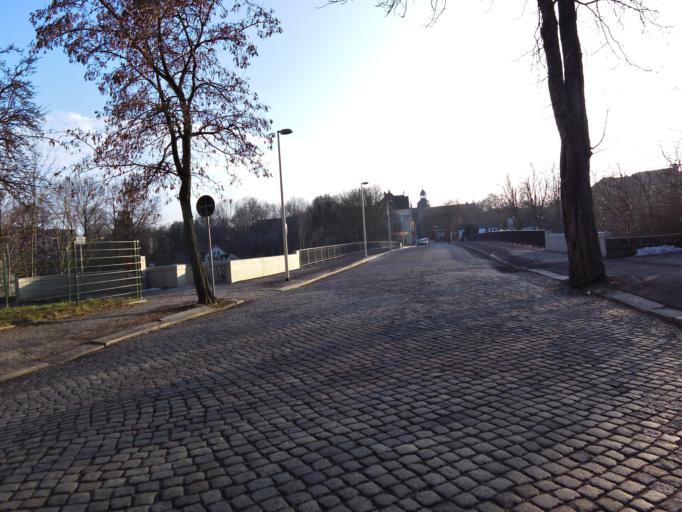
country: DE
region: Saxony
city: Glauchau
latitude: 50.8243
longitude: 12.5445
